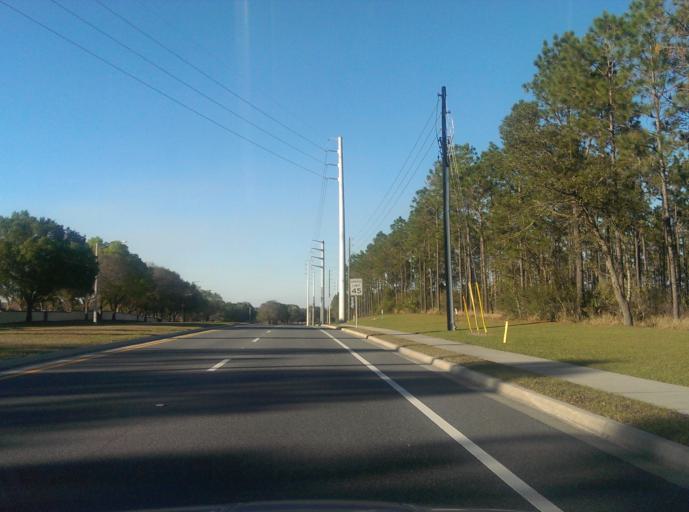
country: US
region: Florida
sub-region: Polk County
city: Loughman
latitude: 28.2976
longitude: -81.5905
